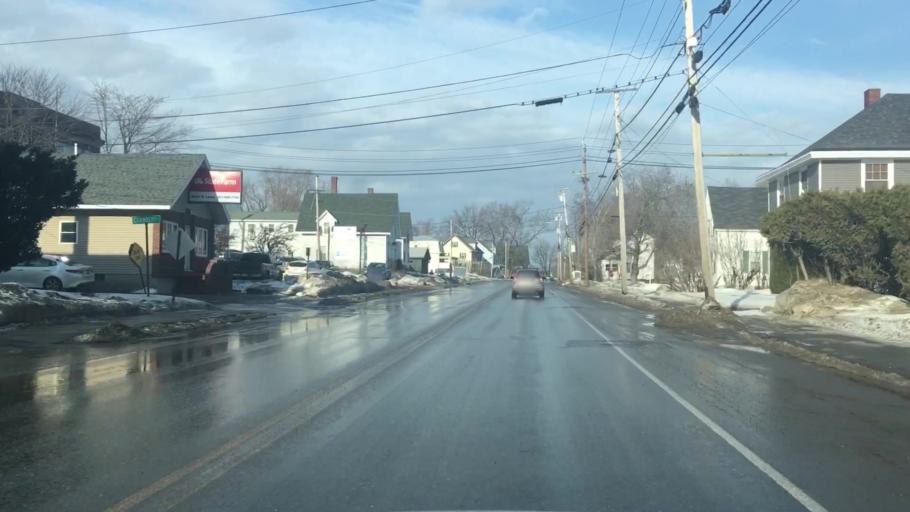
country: US
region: Maine
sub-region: Penobscot County
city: Bangor
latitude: 44.7741
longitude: -68.7796
